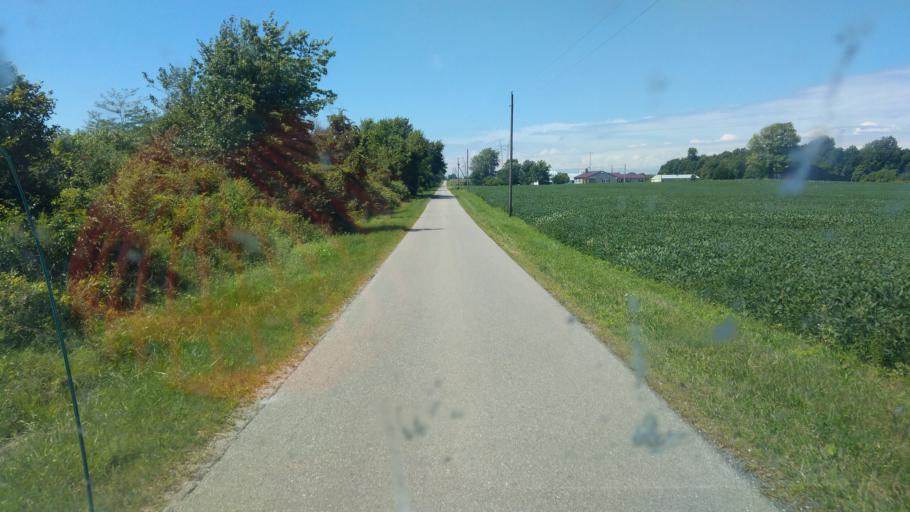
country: US
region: Ohio
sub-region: Crawford County
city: Bucyrus
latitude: 40.8125
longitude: -83.0289
